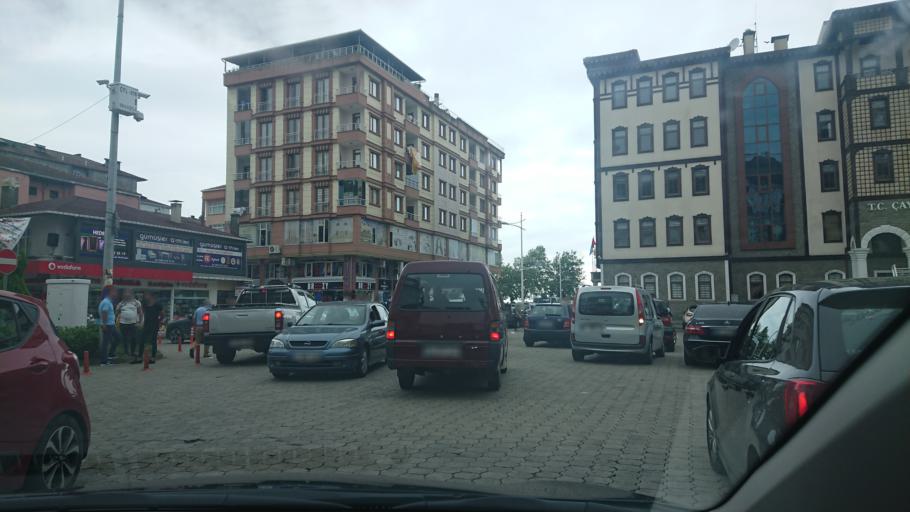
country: TR
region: Rize
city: Cayeli
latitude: 41.0890
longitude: 40.7254
